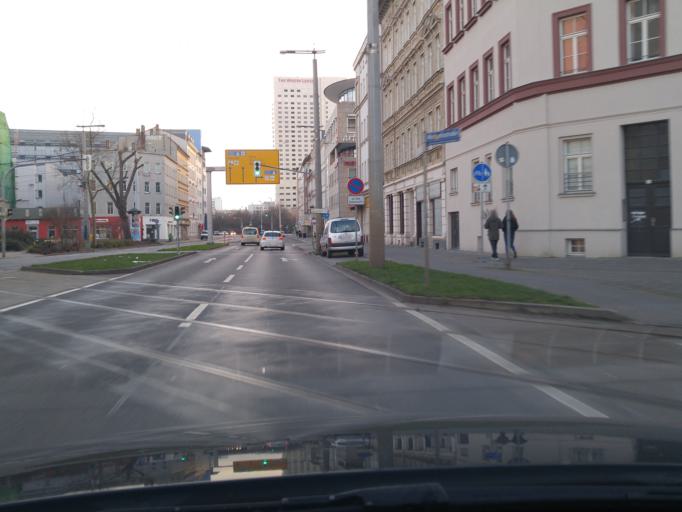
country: DE
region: Saxony
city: Leipzig
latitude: 51.3505
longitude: 12.3764
